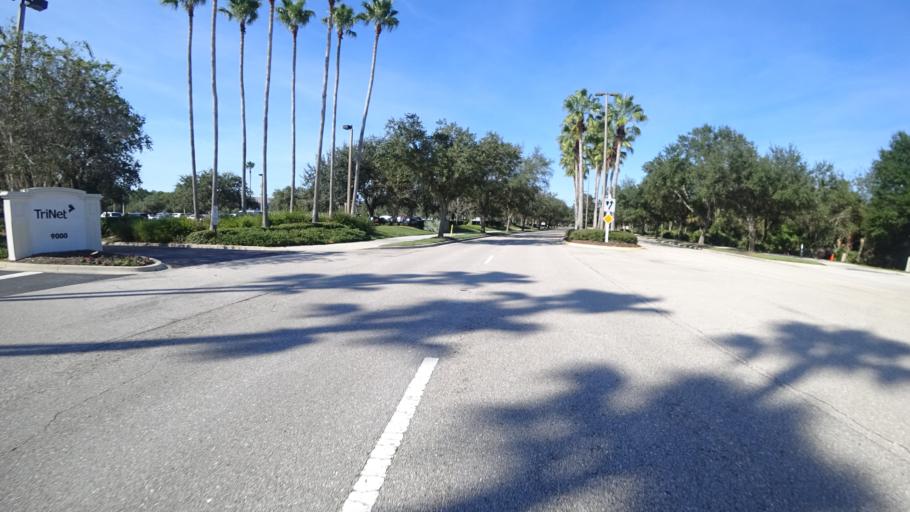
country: US
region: Florida
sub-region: Sarasota County
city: The Meadows
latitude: 27.3959
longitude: -82.4479
